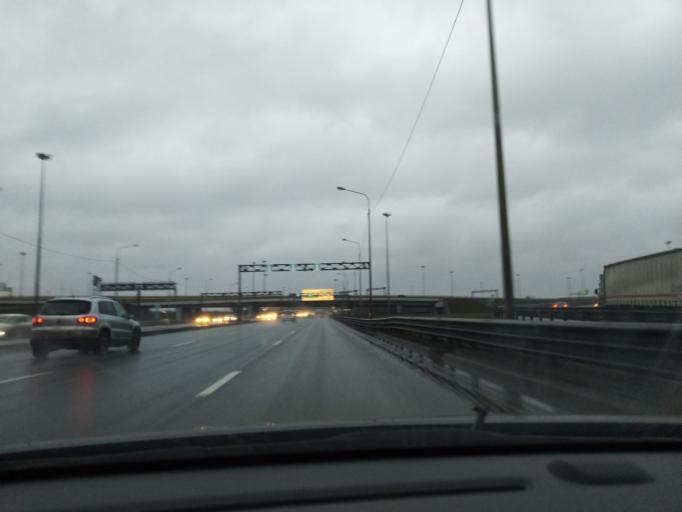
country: RU
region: St.-Petersburg
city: Sosnovaya Polyana
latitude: 59.7974
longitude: 30.1540
